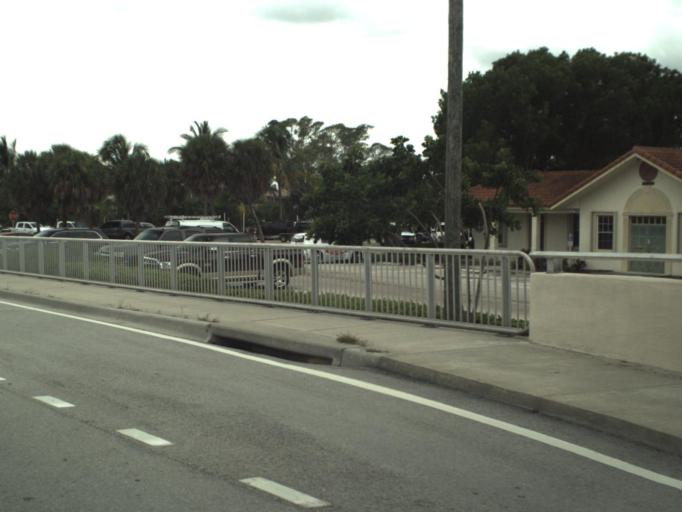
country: US
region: Florida
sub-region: Palm Beach County
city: Jupiter
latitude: 26.9413
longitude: -80.0843
